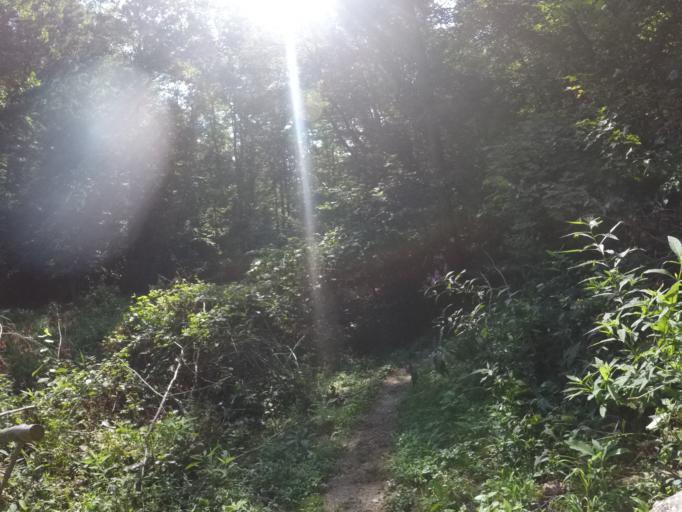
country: US
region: Ohio
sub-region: Lawrence County
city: Ironton
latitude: 38.6158
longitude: -82.6221
